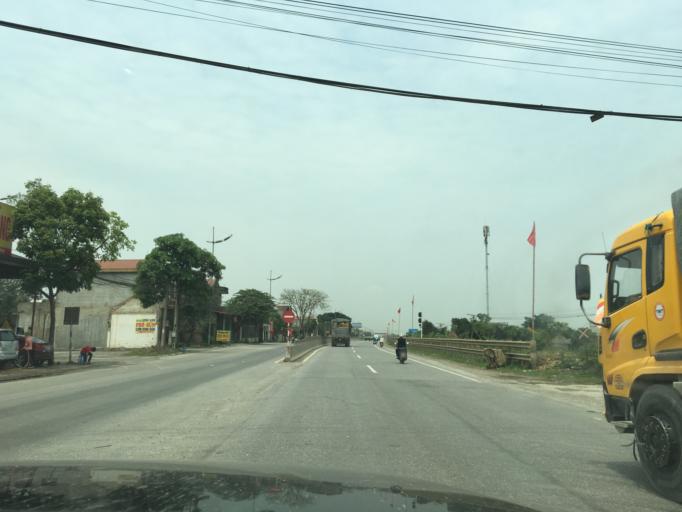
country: VN
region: Ninh Binh
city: Thi Tran Tam Diep
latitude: 20.1713
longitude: 105.9429
